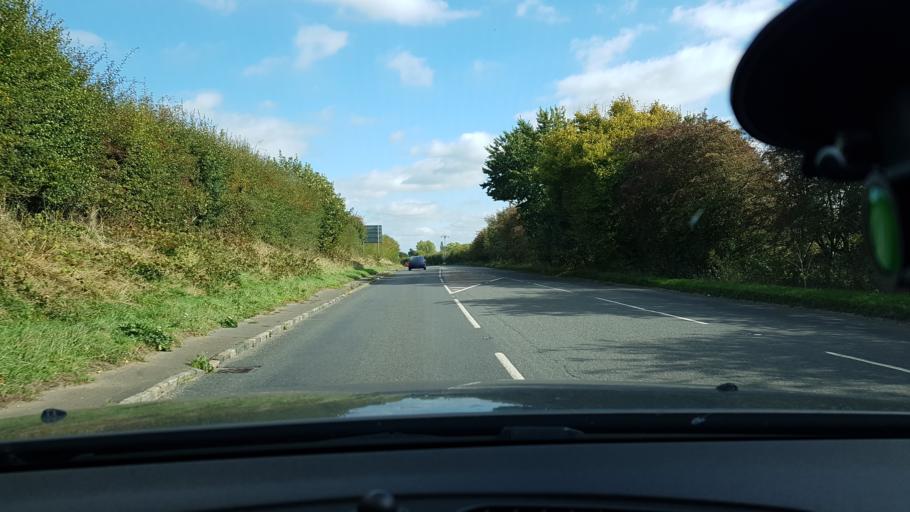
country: GB
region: England
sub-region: West Berkshire
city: Hungerford
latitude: 51.4156
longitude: -1.4929
